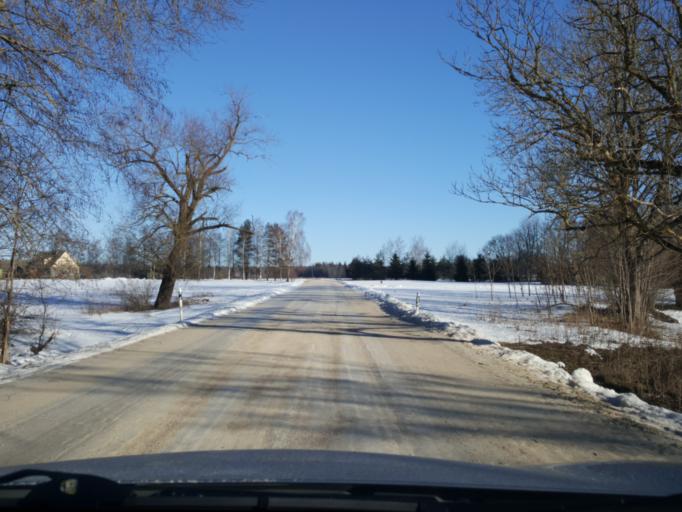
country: EE
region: Viljandimaa
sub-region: Suure-Jaani vald
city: Suure-Jaani
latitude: 58.4535
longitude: 25.5351
